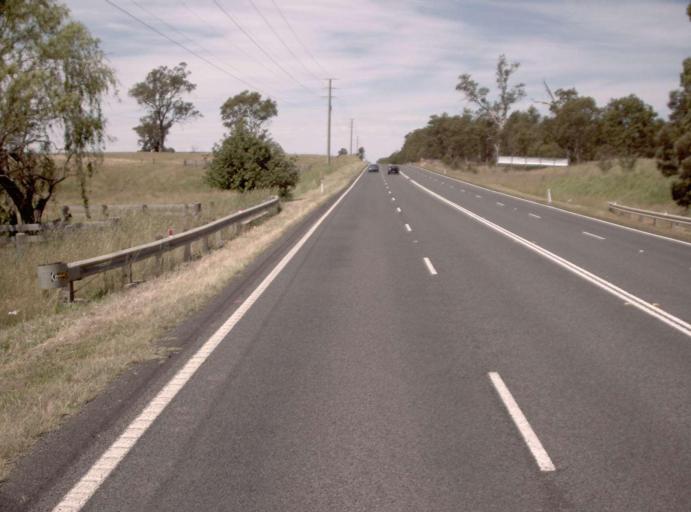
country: AU
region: Victoria
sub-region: Latrobe
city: Traralgon
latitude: -38.1768
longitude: 146.6417
